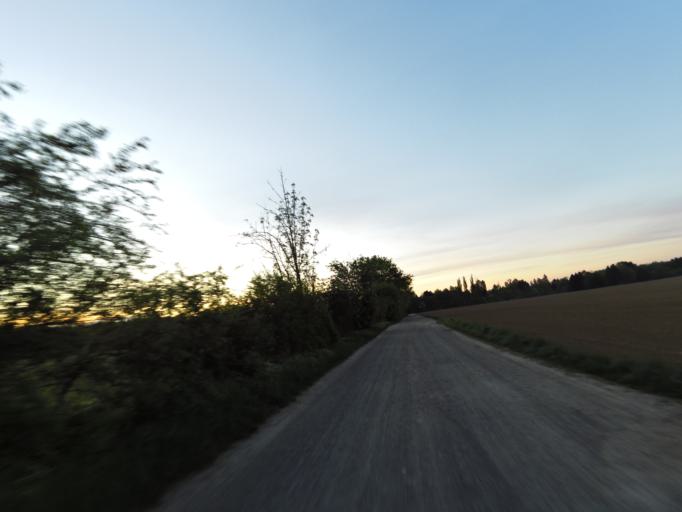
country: DE
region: North Rhine-Westphalia
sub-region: Regierungsbezirk Koln
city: Wachtberg
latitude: 50.6817
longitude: 7.0615
